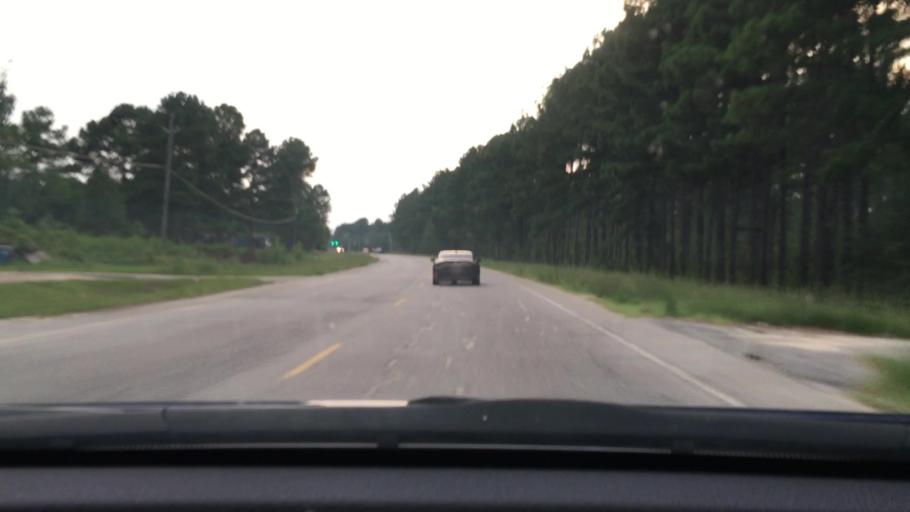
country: US
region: South Carolina
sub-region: Sumter County
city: Cherryvale
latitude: 33.9367
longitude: -80.4477
